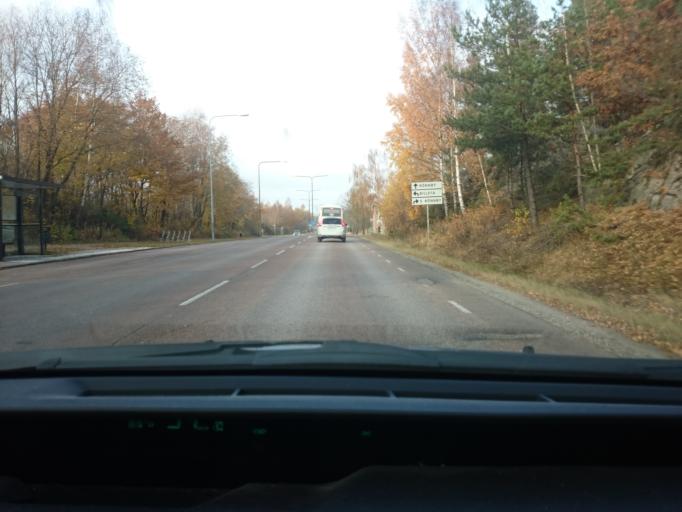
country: SE
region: Vaestmanland
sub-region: Vasteras
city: Vasteras
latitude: 59.6395
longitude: 16.5087
